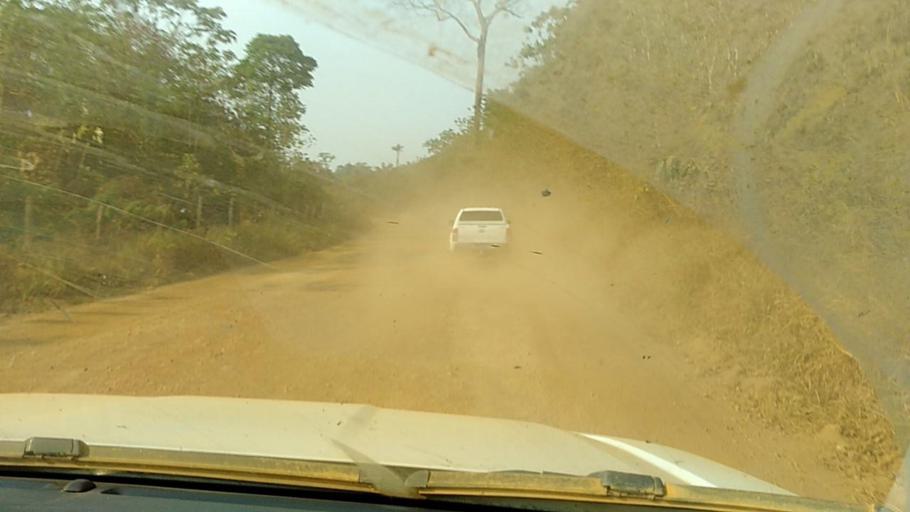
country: BR
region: Rondonia
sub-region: Porto Velho
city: Porto Velho
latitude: -8.7454
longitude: -63.9644
